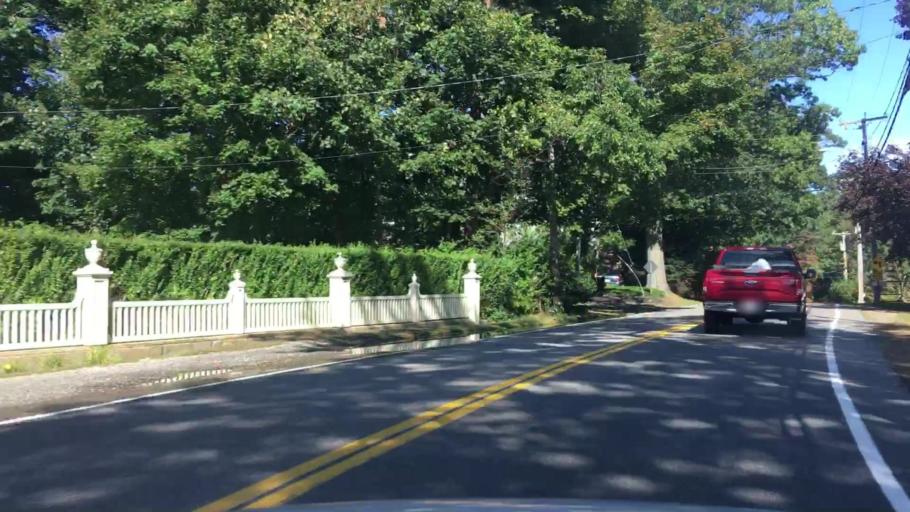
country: US
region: Maine
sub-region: York County
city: Kittery Point
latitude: 43.0816
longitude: -70.7158
